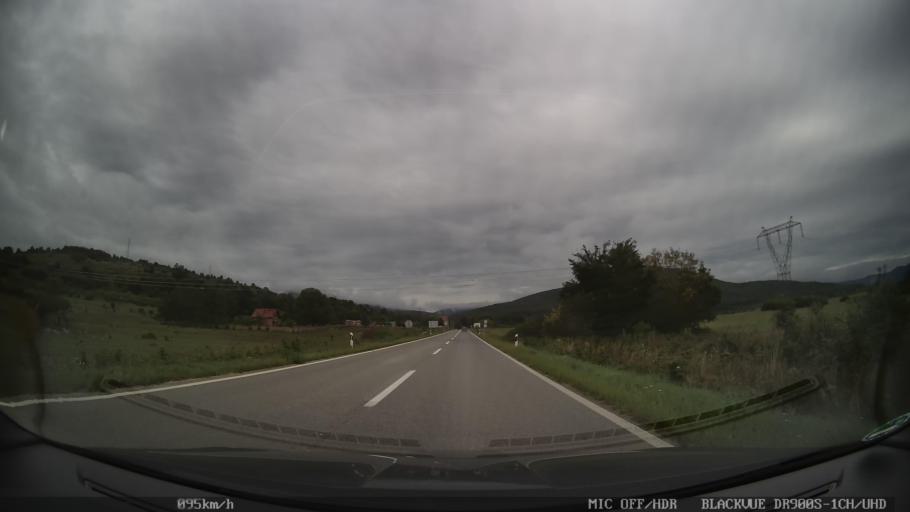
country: HR
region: Licko-Senjska
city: Otocac
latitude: 44.8579
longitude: 15.3215
